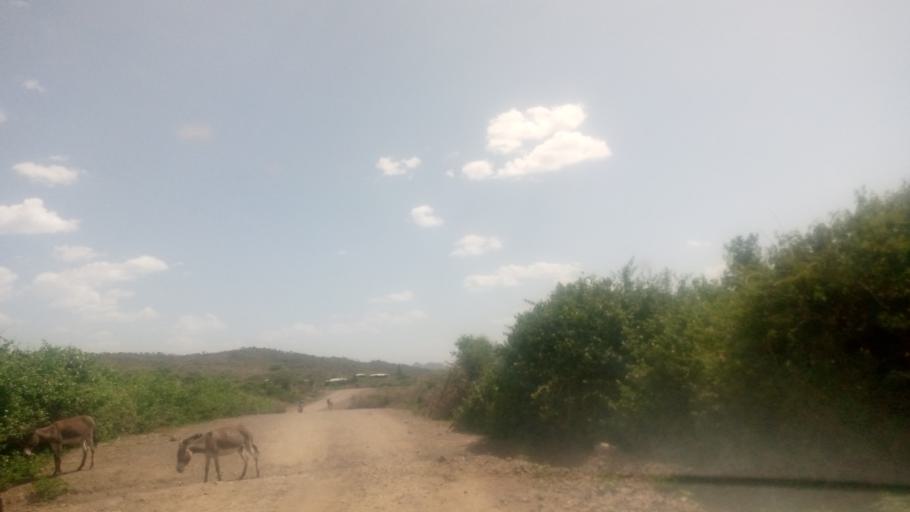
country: ET
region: Oromiya
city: Deder
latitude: 9.5173
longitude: 41.3340
